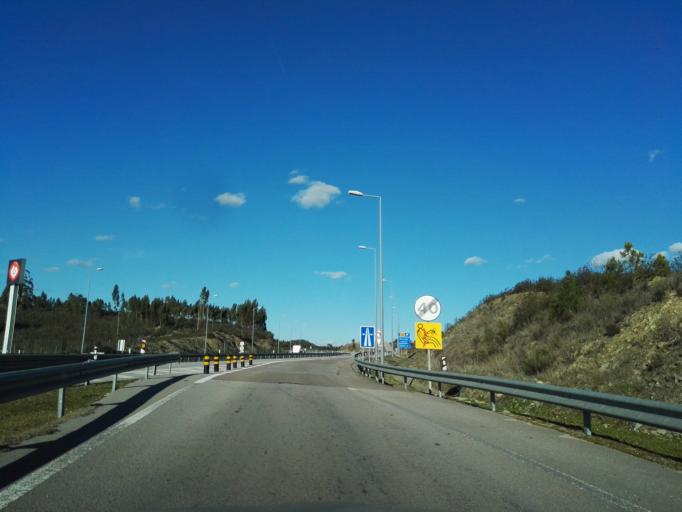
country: PT
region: Portalegre
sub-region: Nisa
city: Nisa
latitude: 39.5739
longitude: -7.7814
